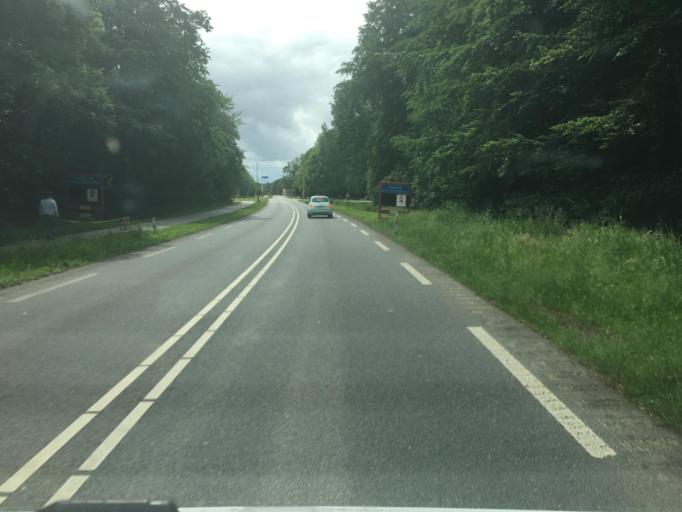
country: NL
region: Flevoland
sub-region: Gemeente Noordoostpolder
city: Emmeloord
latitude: 52.6484
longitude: 5.7219
